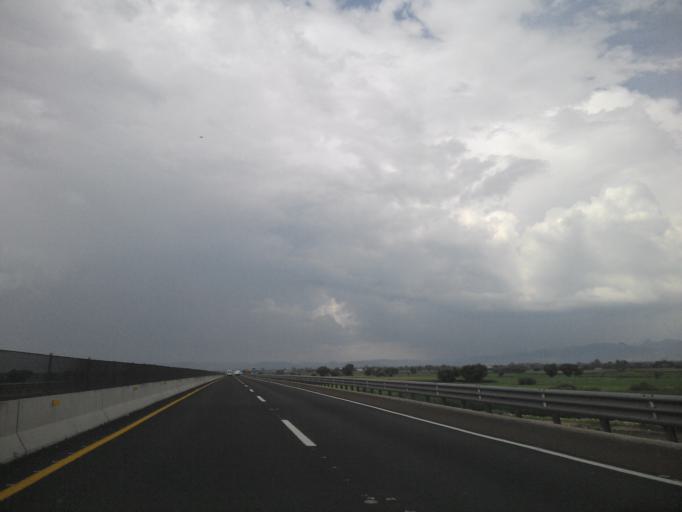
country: MX
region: Hidalgo
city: El Llano
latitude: 20.0886
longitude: -99.3158
